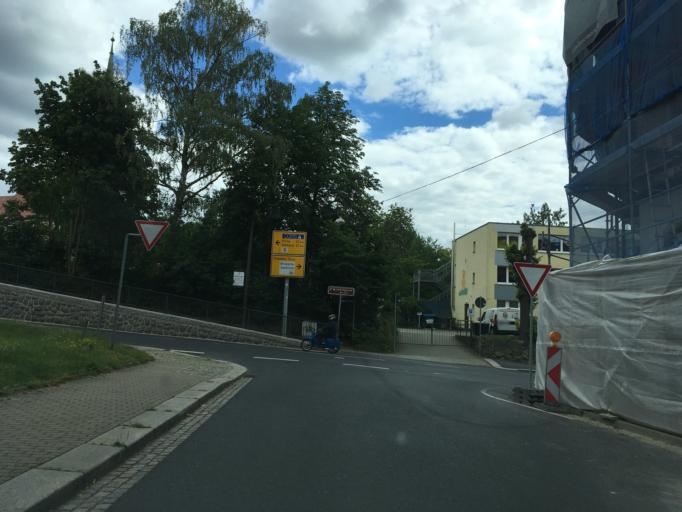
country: DE
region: Saxony
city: Radeberg
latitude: 51.1186
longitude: 13.9185
